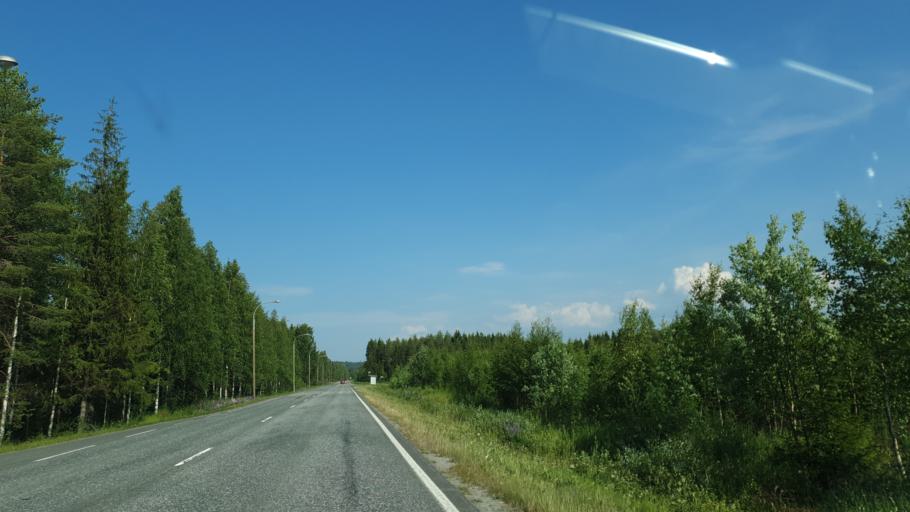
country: FI
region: Northern Savo
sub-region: Kuopio
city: Nilsiae
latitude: 63.1422
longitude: 27.9098
